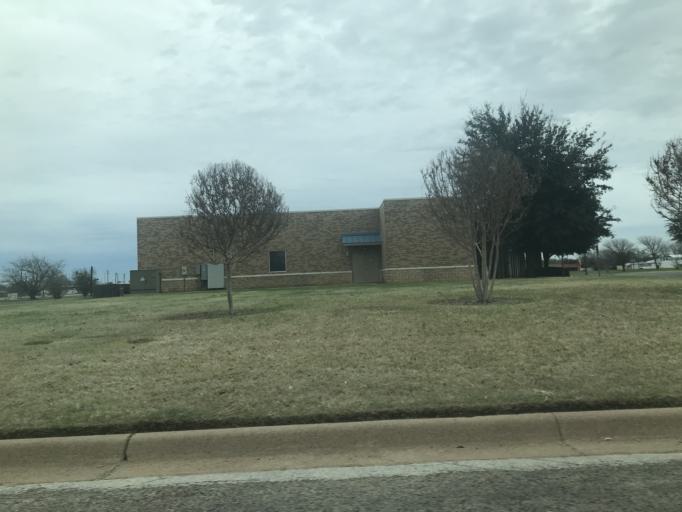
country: US
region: Texas
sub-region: Taylor County
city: Abilene
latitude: 32.4706
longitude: -99.7286
